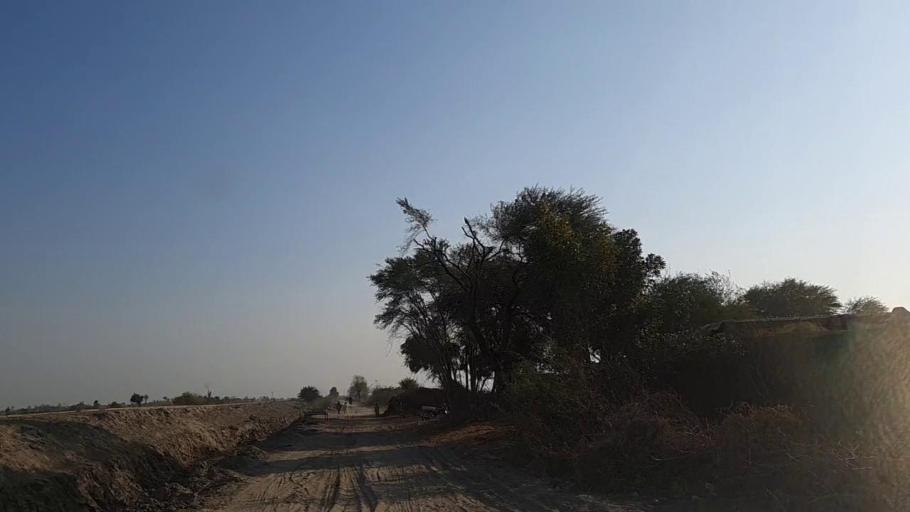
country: PK
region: Sindh
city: Daur
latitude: 26.4416
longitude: 68.3513
